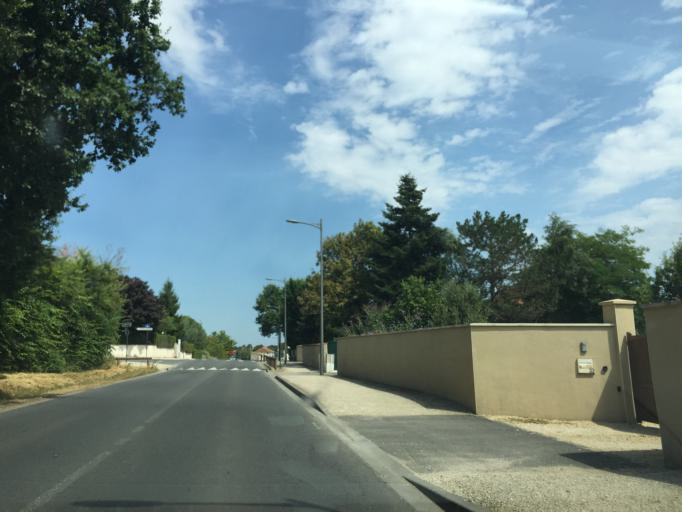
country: FR
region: Poitou-Charentes
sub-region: Departement de la Vienne
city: Biard
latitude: 46.5552
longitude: 0.3025
